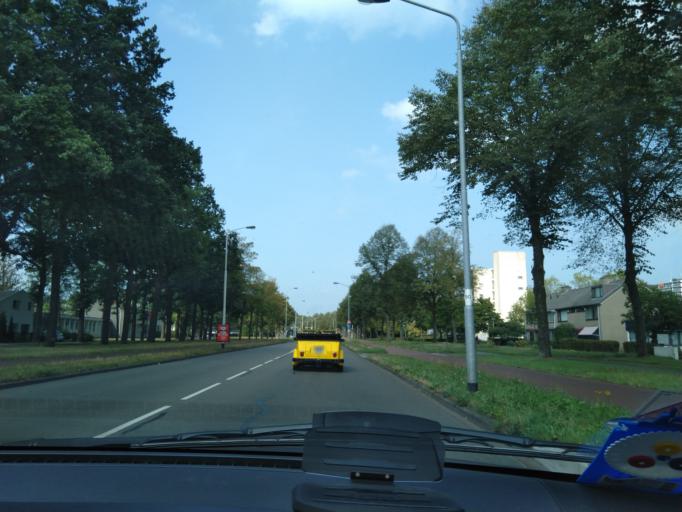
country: NL
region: North Brabant
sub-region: Gemeente Breda
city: Hoge Vucht
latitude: 51.5856
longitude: 4.8201
